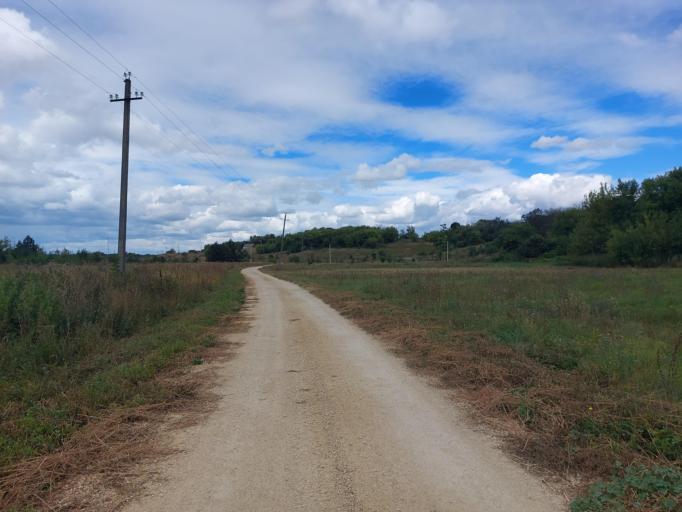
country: RU
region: Lipetsk
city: Terbuny
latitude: 52.2667
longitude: 38.2052
